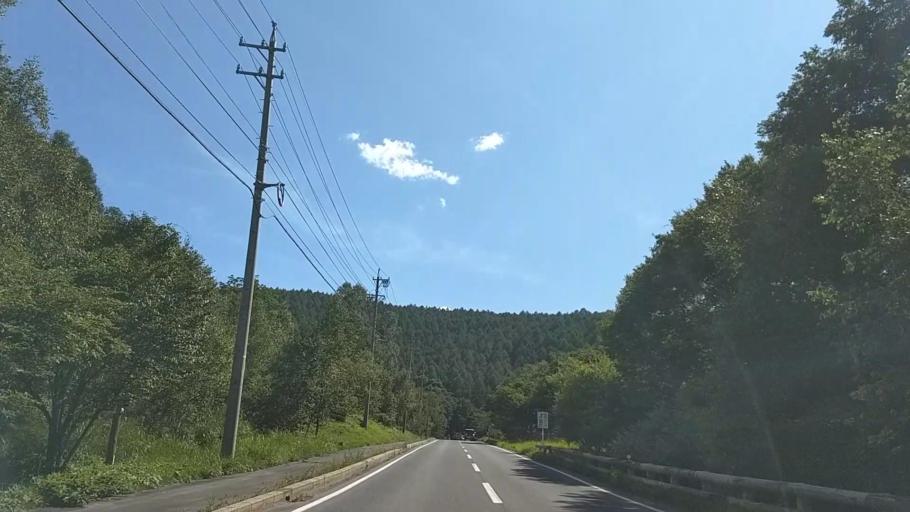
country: JP
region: Nagano
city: Chino
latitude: 36.1135
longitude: 138.2610
